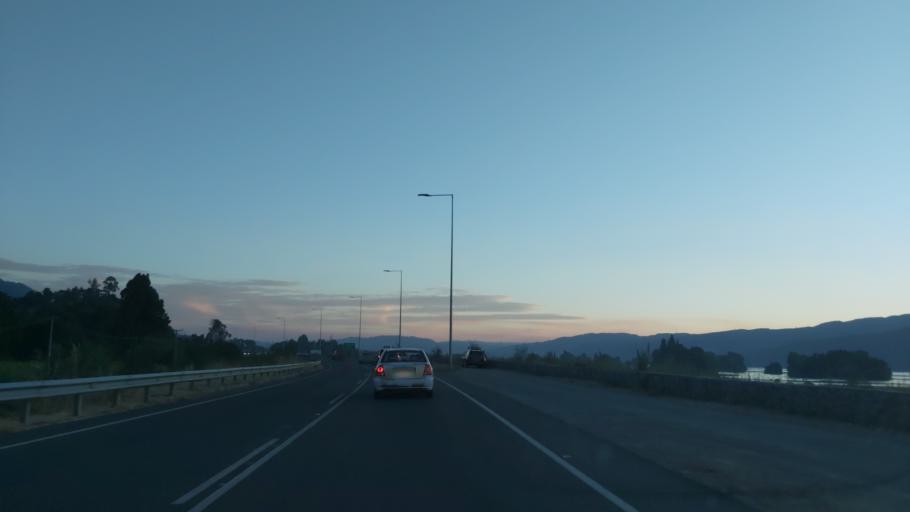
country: CL
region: Biobio
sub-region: Provincia de Concepcion
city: Chiguayante
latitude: -36.8868
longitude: -73.0382
